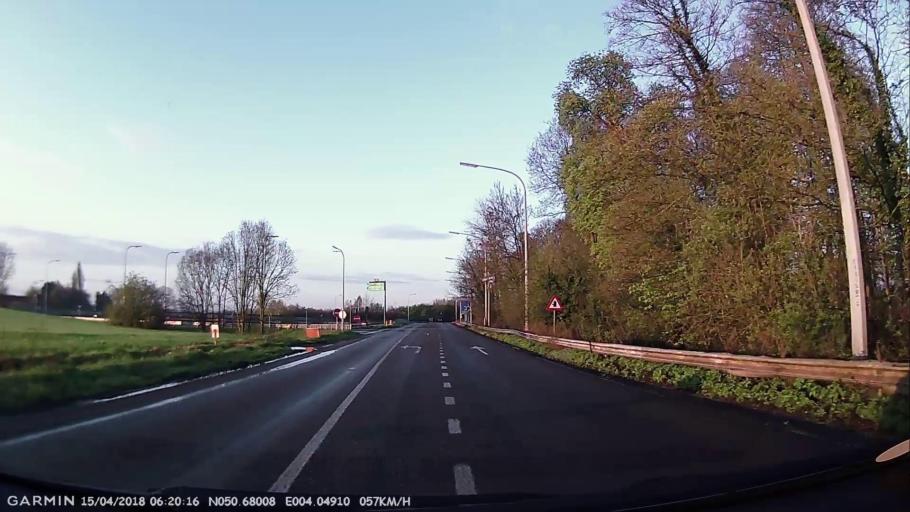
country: BE
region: Wallonia
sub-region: Province du Hainaut
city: Enghien
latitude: 50.6799
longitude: 4.0490
